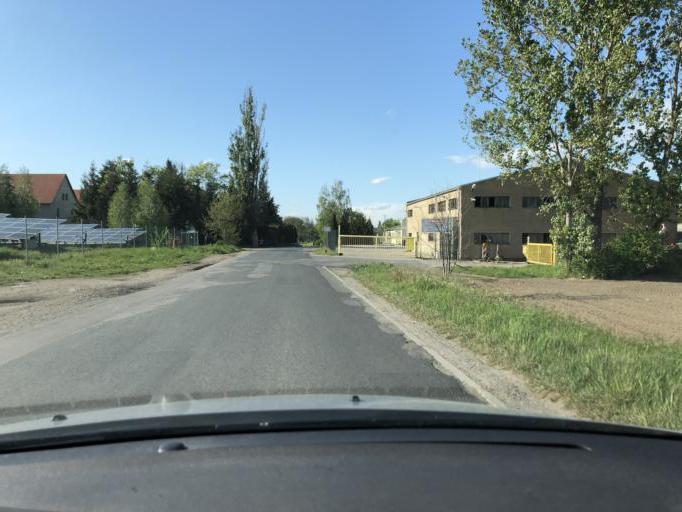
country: DE
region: Thuringia
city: Gerstenberg
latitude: 51.0136
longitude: 12.4381
